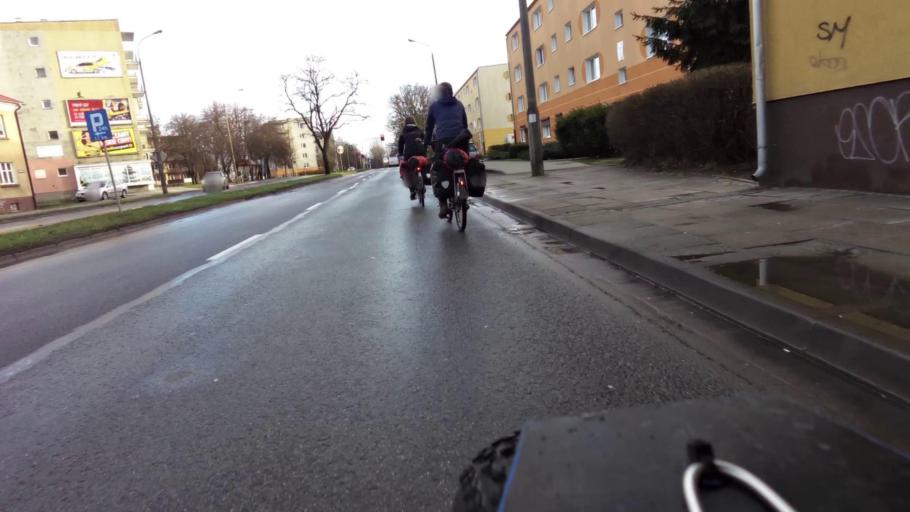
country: PL
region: Lubusz
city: Gorzow Wielkopolski
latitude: 52.7347
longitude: 15.2099
